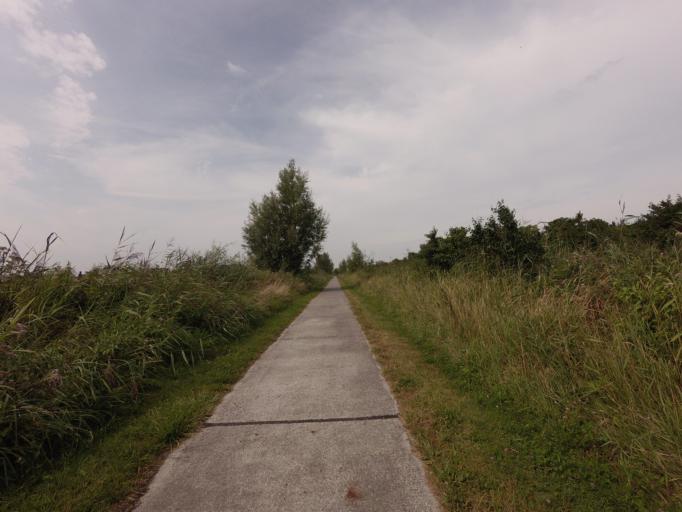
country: NL
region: Flevoland
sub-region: Gemeente Almere
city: Almere Stad
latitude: 52.4001
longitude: 5.1769
